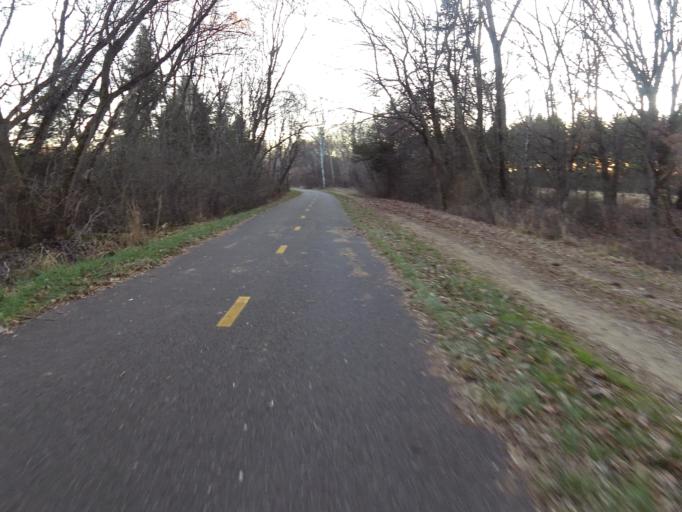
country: US
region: Minnesota
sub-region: Washington County
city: Grant
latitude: 45.0898
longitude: -92.8909
